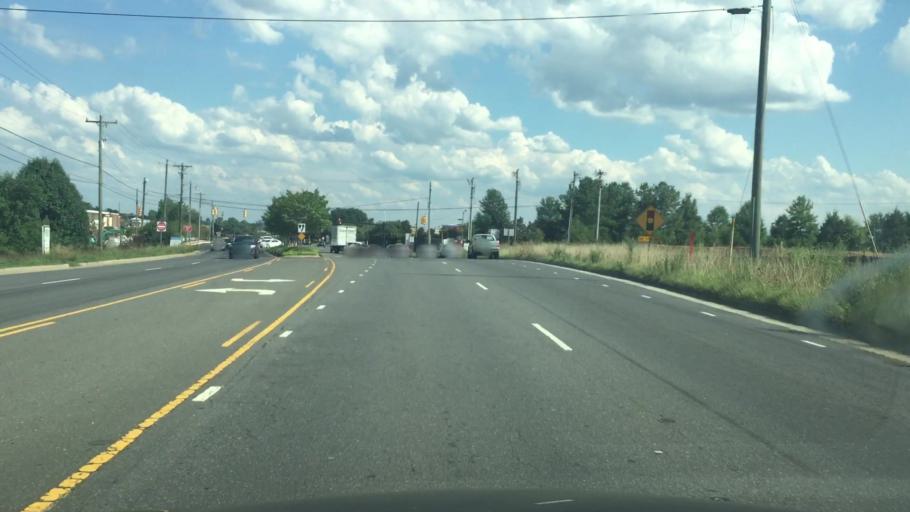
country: US
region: North Carolina
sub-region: Cabarrus County
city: Kannapolis
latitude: 35.4234
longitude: -80.6774
